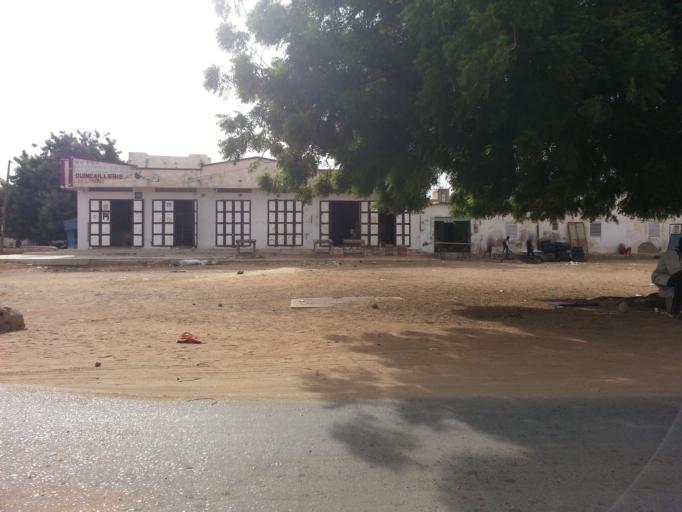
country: SN
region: Diourbel
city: Touba
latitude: 14.8623
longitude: -15.8599
